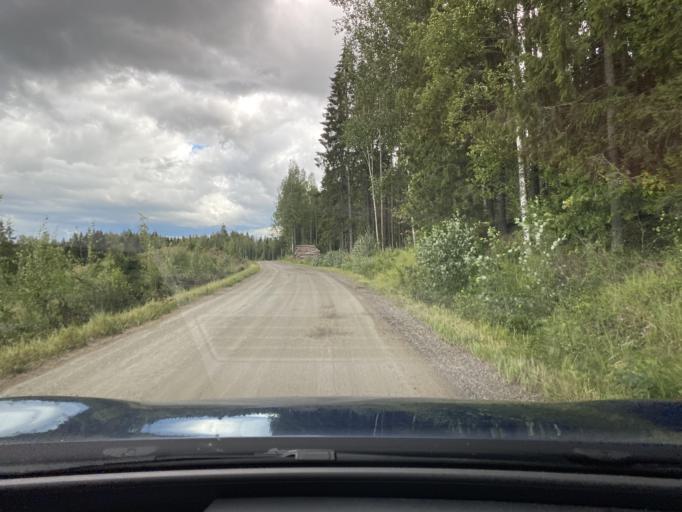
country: FI
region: Pirkanmaa
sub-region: Lounais-Pirkanmaa
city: Punkalaidun
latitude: 61.2258
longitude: 23.1562
